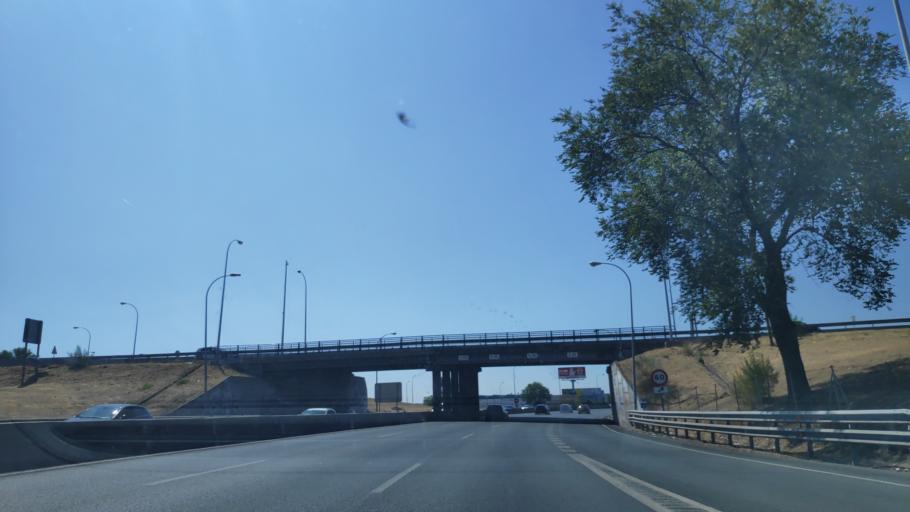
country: ES
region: Madrid
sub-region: Provincia de Madrid
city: Getafe
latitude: 40.2965
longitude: -3.7377
